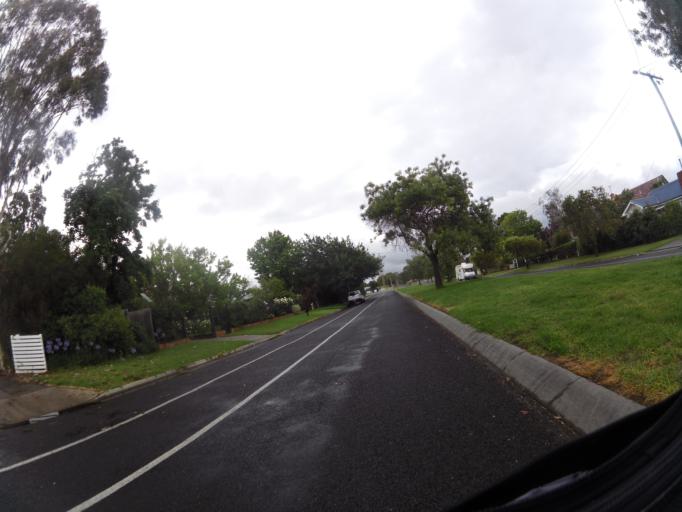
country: AU
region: Victoria
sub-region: East Gippsland
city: Bairnsdale
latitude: -37.8307
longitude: 147.6270
